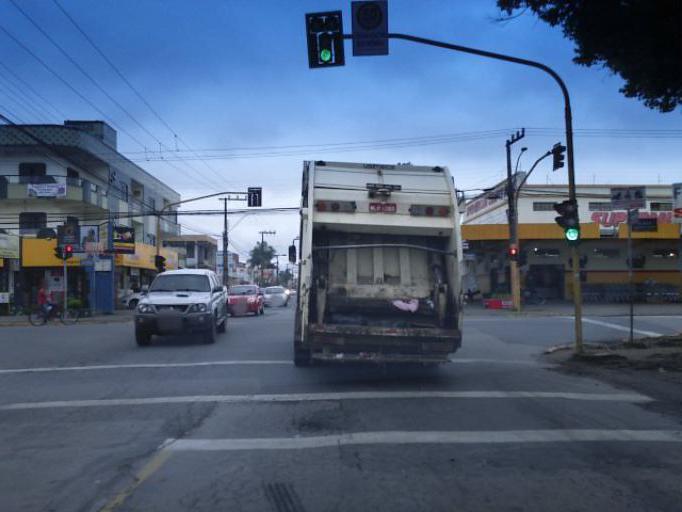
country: BR
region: Santa Catarina
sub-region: Itajai
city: Itajai
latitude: -26.9048
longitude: -48.7003
